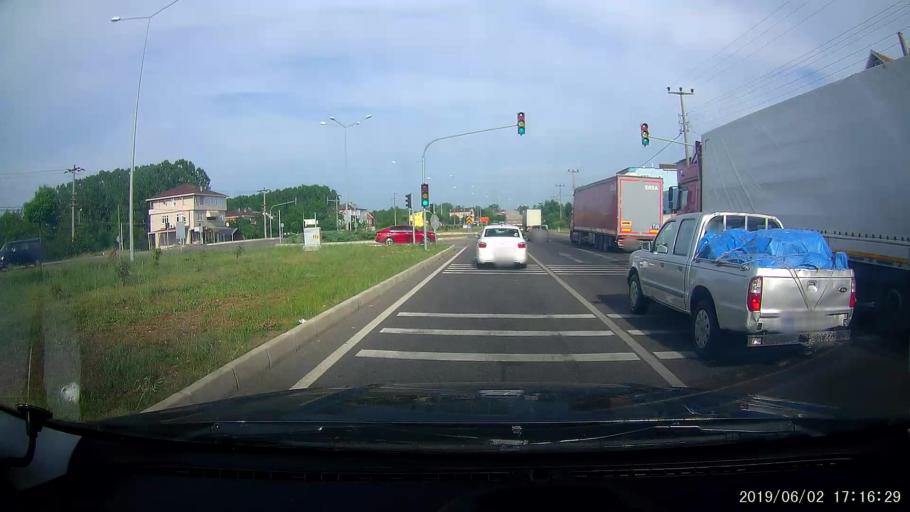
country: TR
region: Samsun
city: Dikbiyik
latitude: 41.2340
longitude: 36.5676
